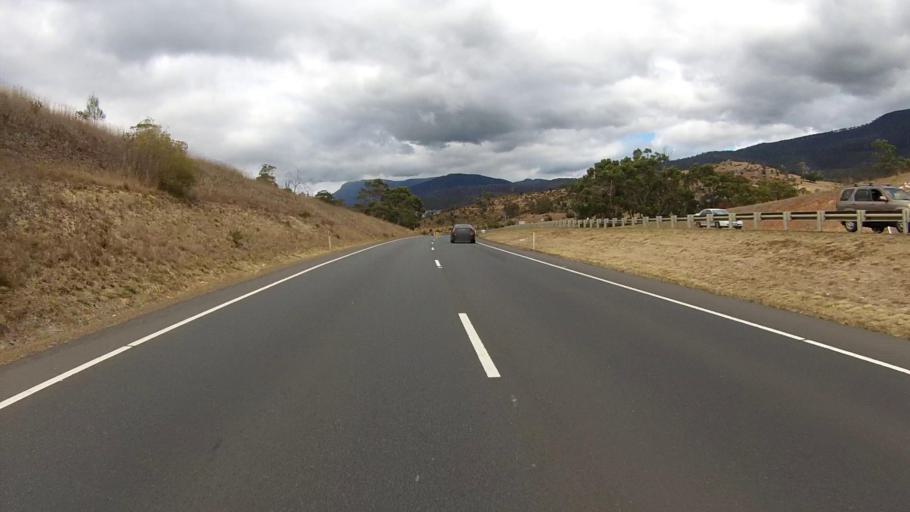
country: AU
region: Tasmania
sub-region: Glenorchy
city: Claremont
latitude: -42.7750
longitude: 147.2391
